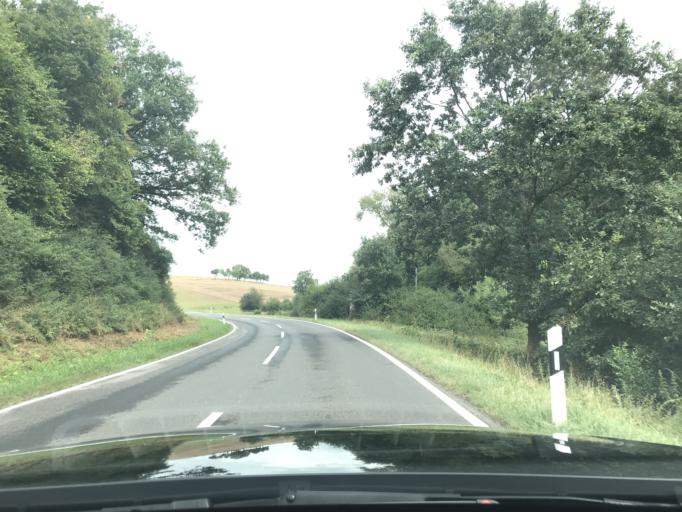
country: DE
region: Bavaria
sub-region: Regierungsbezirk Unterfranken
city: Eltmann
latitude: 49.9320
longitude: 10.6636
